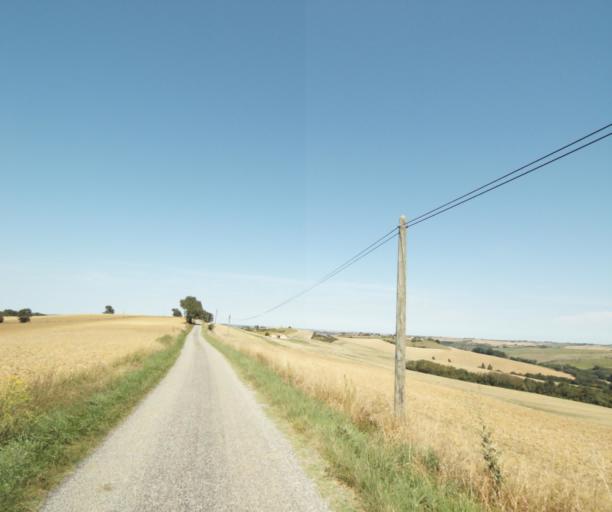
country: FR
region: Midi-Pyrenees
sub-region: Departement de l'Ariege
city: Lezat-sur-Leze
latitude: 43.2623
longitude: 1.3858
